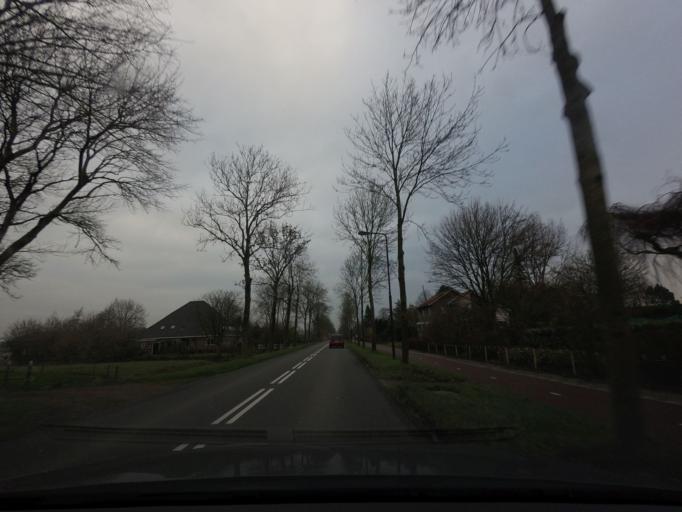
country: NL
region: North Holland
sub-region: Gemeente Heerhugowaard
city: Heerhugowaard
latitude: 52.7126
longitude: 4.8524
